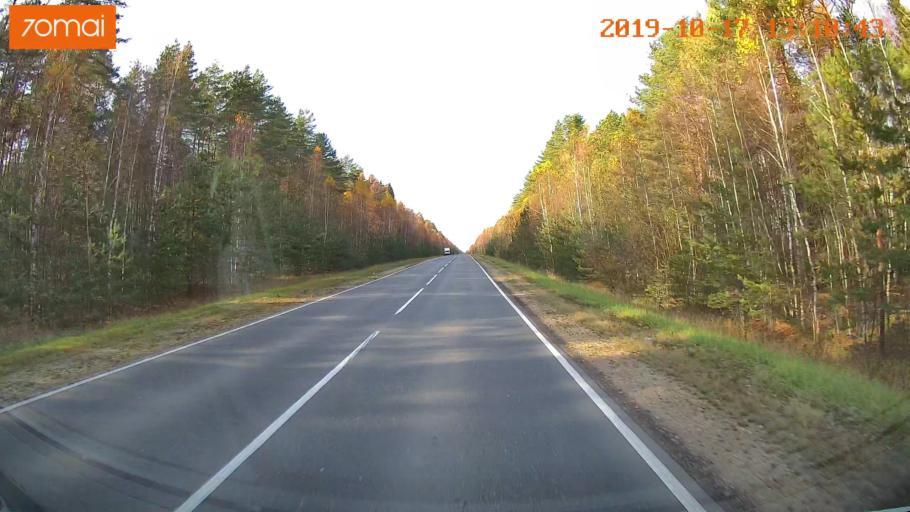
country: RU
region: Rjazan
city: Syntul
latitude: 55.0214
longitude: 41.2515
